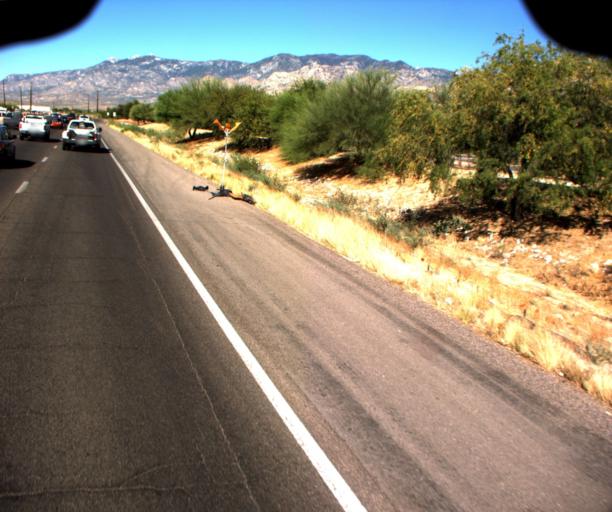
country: US
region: Arizona
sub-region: Pima County
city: Oro Valley
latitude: 32.4064
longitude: -110.9464
